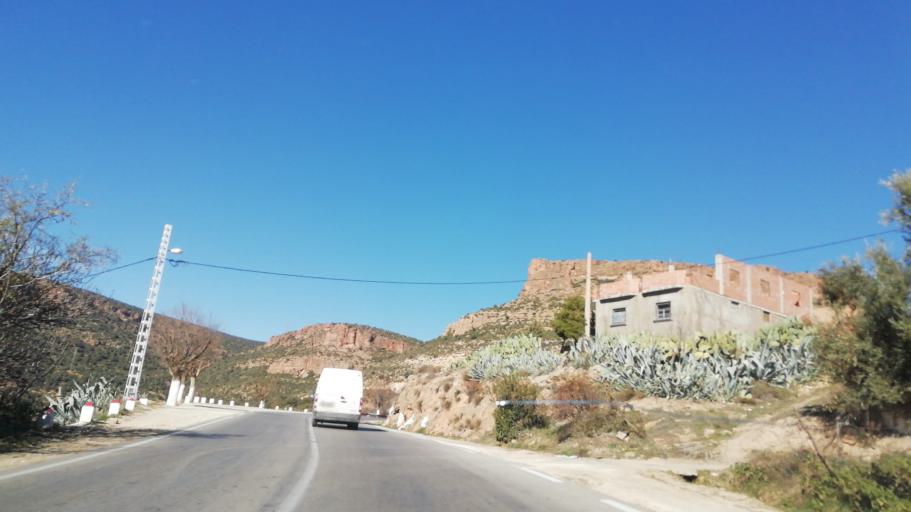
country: DZ
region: Tlemcen
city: Sebdou
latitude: 34.6852
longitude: -1.3177
